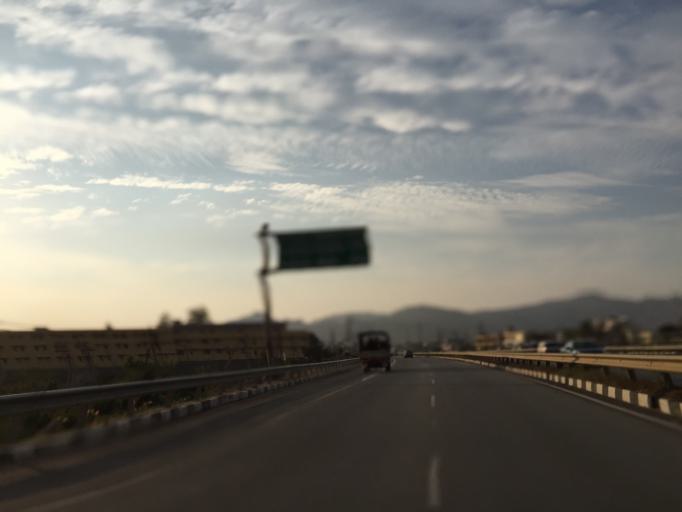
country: IN
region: Karnataka
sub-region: Kolar
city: Kolar
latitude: 13.1222
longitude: 78.1247
